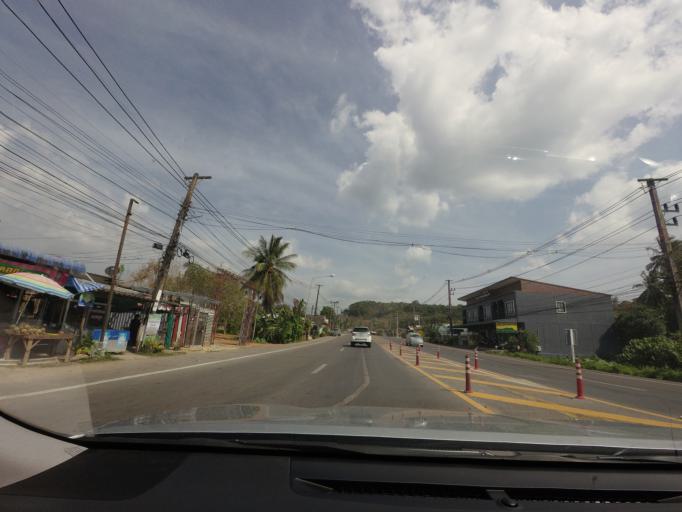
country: TH
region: Phangnga
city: Ban Ao Nang
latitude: 8.0527
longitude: 98.7641
